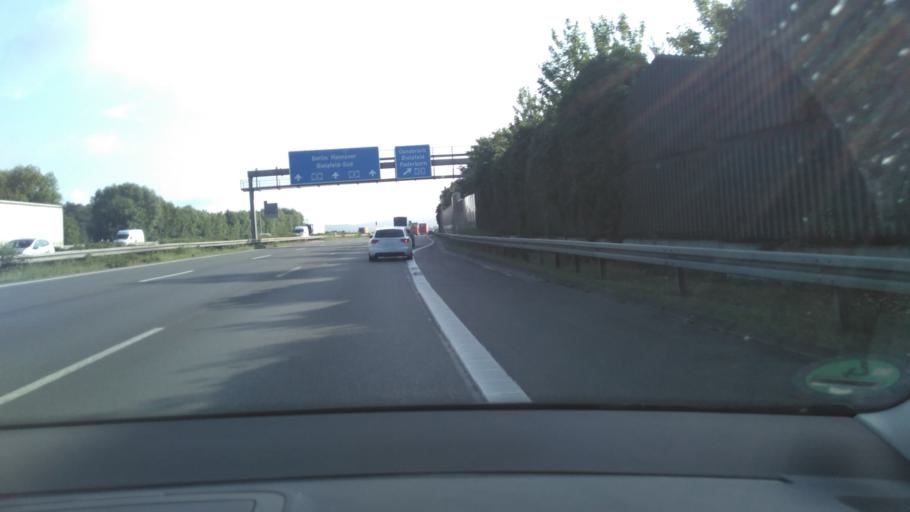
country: DE
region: North Rhine-Westphalia
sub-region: Regierungsbezirk Detmold
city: Verl
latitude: 51.9381
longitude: 8.5366
